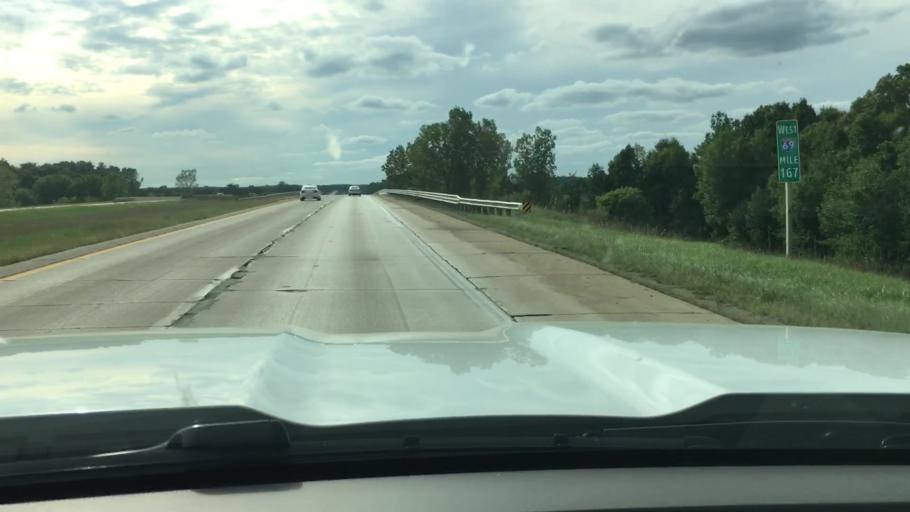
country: US
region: Michigan
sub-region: Lapeer County
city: Imlay City
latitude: 42.9978
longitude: -83.1007
